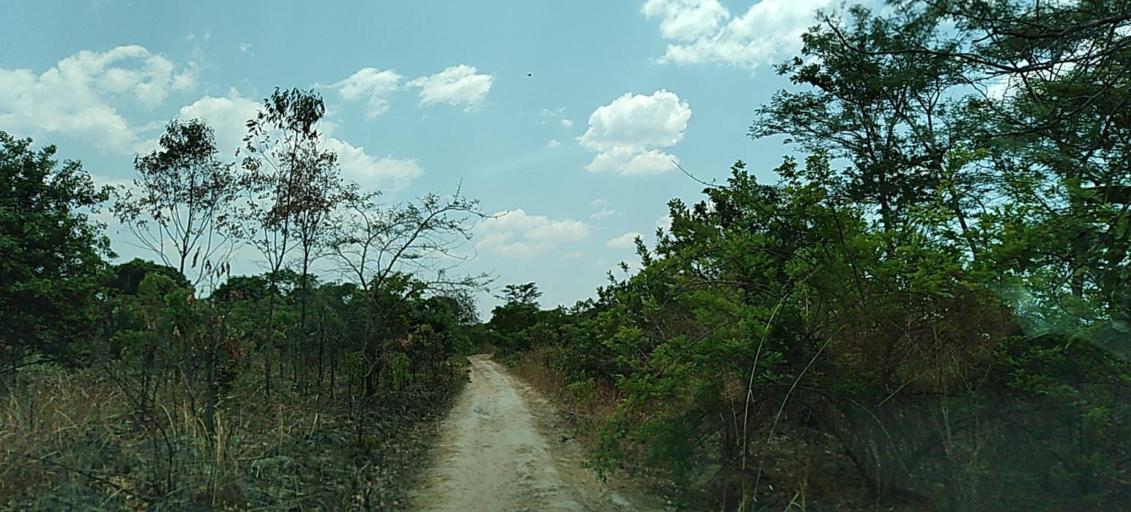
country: ZM
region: Copperbelt
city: Chililabombwe
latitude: -12.4593
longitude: 27.6701
